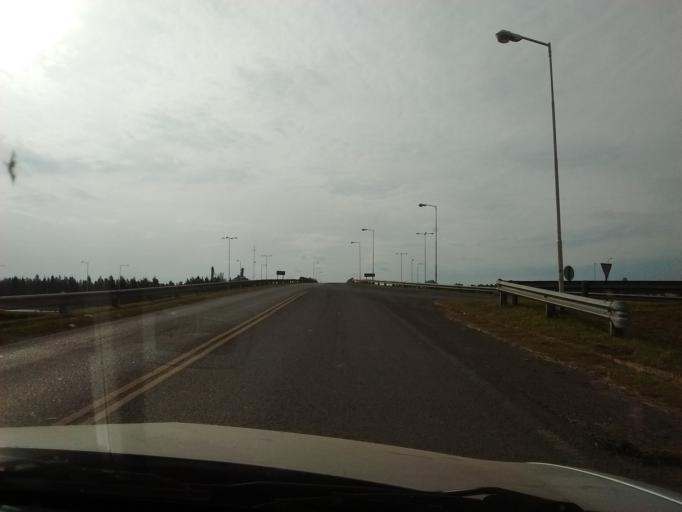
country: AR
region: Santa Fe
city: Funes
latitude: -32.9411
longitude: -60.8197
